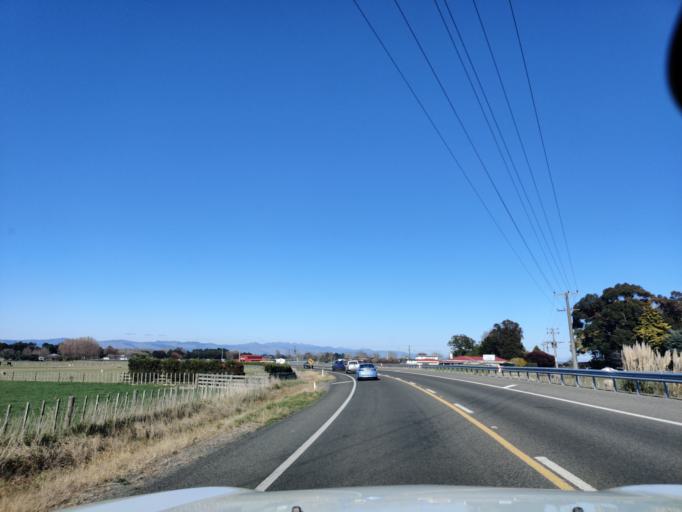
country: NZ
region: Manawatu-Wanganui
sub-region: Palmerston North City
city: Palmerston North
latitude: -40.2775
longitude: 175.5554
